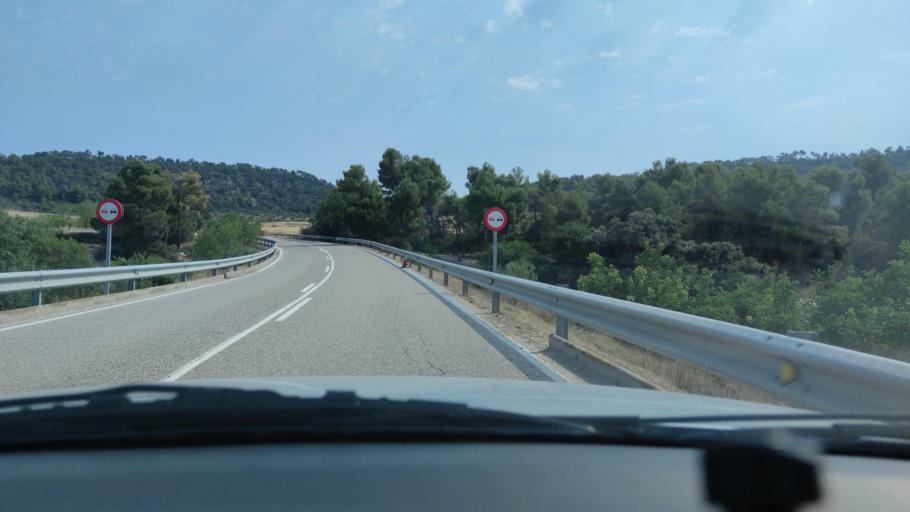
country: ES
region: Catalonia
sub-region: Provincia de Lleida
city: Vallbona de les Monges
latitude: 41.5223
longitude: 1.0313
